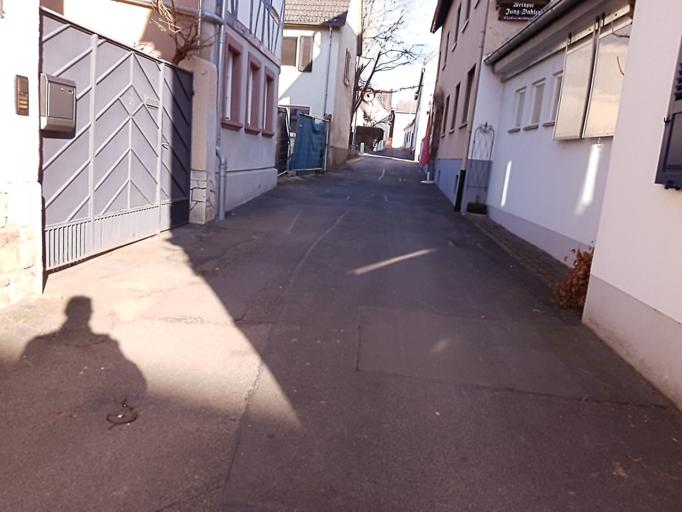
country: DE
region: Hesse
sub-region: Regierungsbezirk Darmstadt
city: Kiedrich
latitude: 50.0209
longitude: 8.0945
